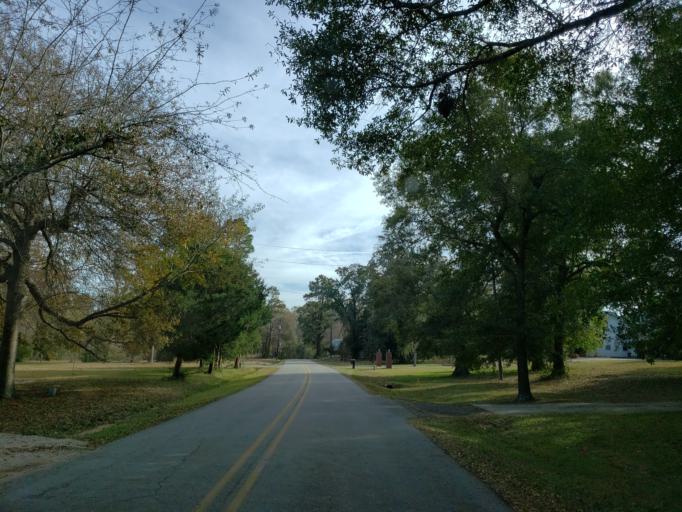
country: US
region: Mississippi
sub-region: Forrest County
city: Rawls Springs
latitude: 31.3800
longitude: -89.3712
